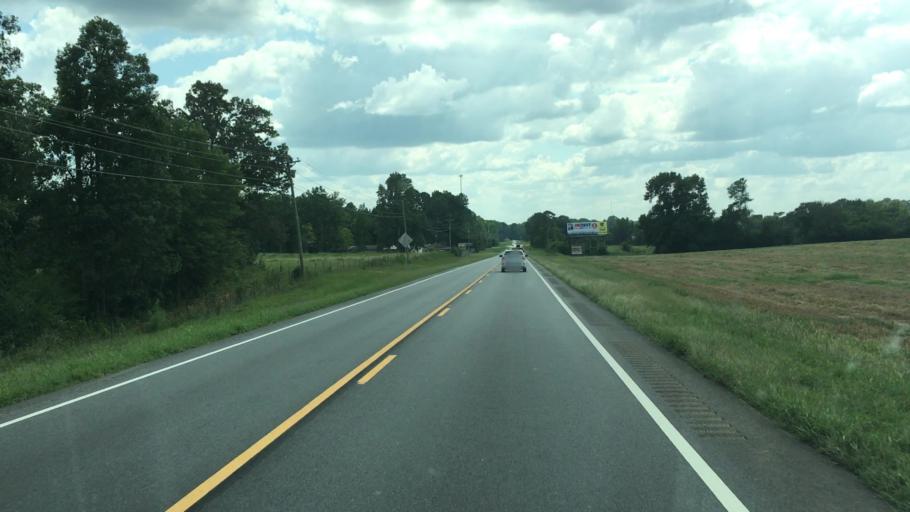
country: US
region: Georgia
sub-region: Putnam County
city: Eatonton
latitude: 33.3906
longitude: -83.3717
